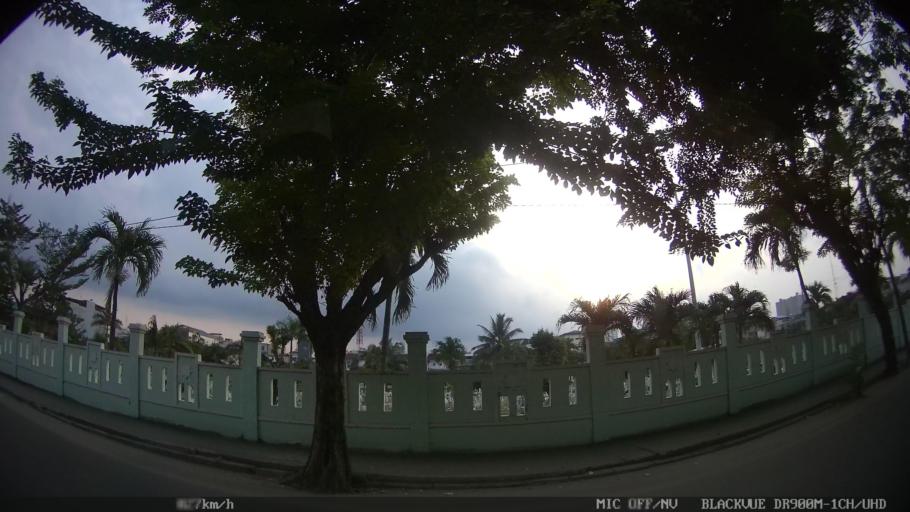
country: ID
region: North Sumatra
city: Medan
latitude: 3.5912
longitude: 98.6895
